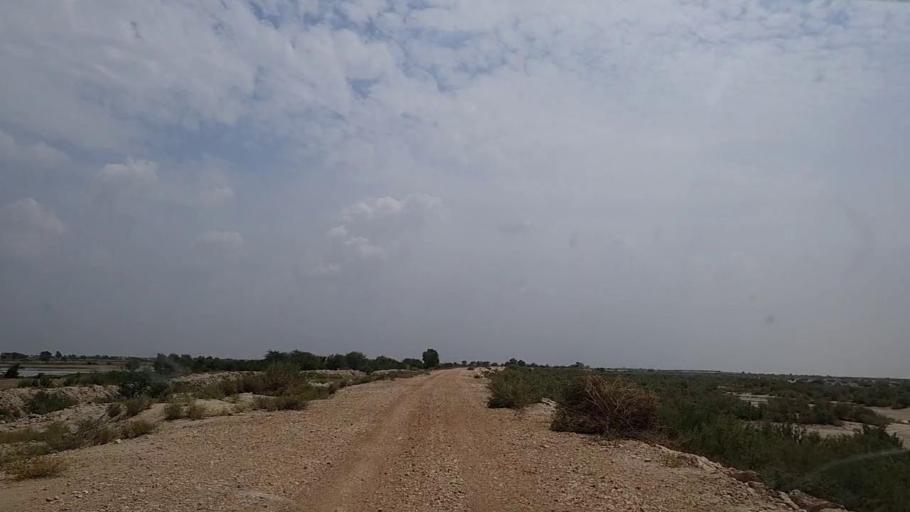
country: PK
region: Sindh
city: Phulji
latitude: 26.8331
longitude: 67.6174
